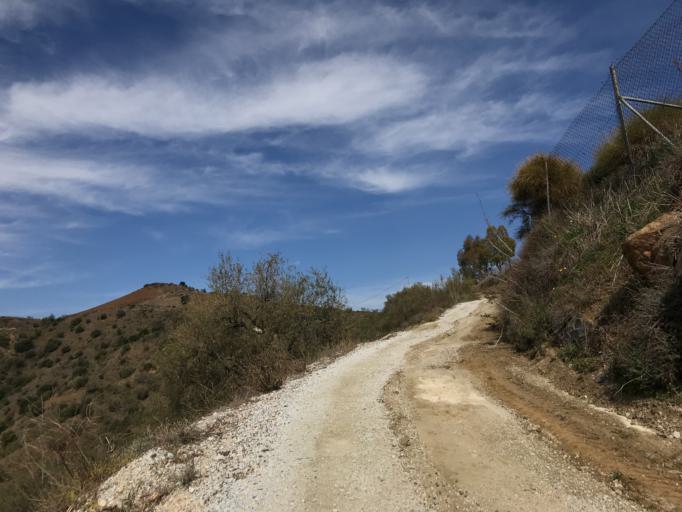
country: ES
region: Andalusia
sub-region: Provincia de Malaga
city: Almachar
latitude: 36.7787
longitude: -4.2179
